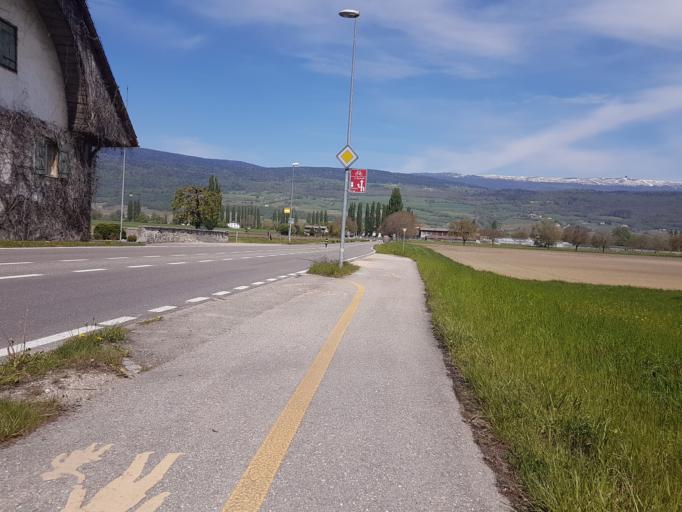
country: CH
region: Neuchatel
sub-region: Neuchatel District
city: Le Landeron
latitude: 47.0401
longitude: 7.0728
